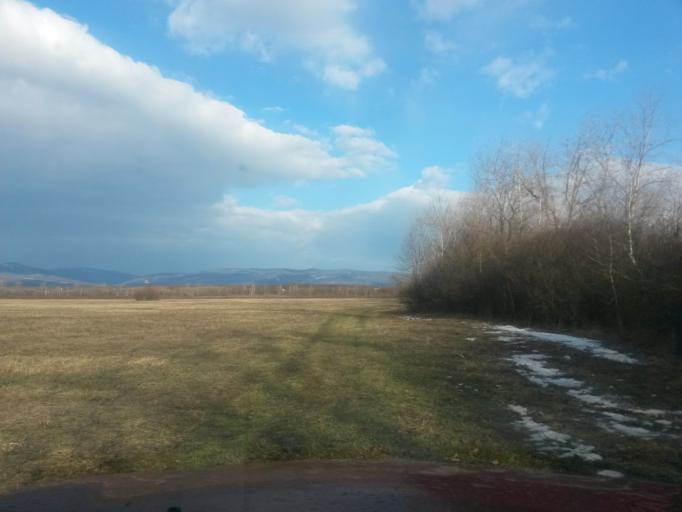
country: SK
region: Kosicky
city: Sobrance
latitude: 48.7804
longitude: 22.0986
